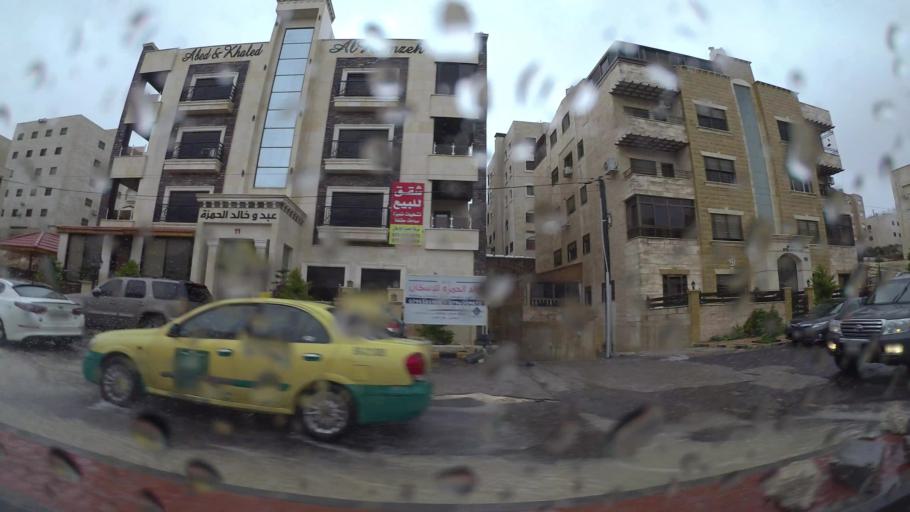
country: JO
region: Amman
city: Al Jubayhah
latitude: 32.0197
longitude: 35.8832
